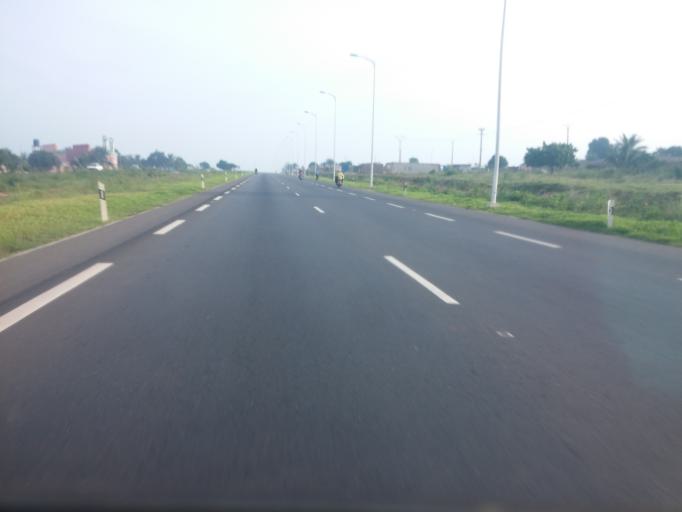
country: TG
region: Maritime
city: Tsevie
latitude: 6.3370
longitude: 1.2161
